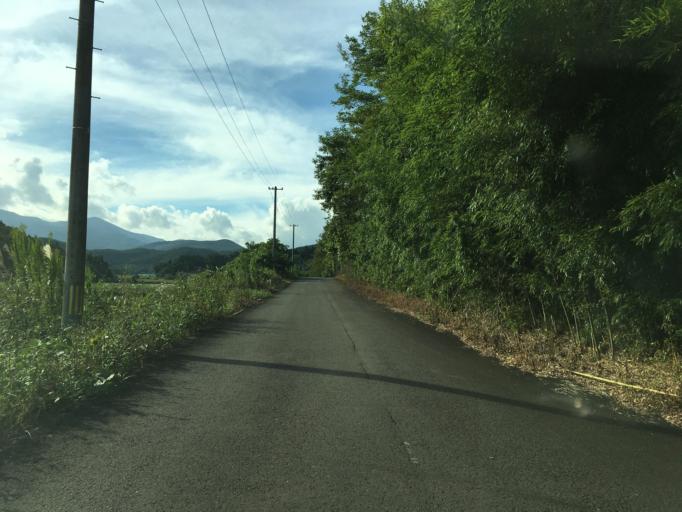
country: JP
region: Fukushima
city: Nihommatsu
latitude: 37.6370
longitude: 140.4075
